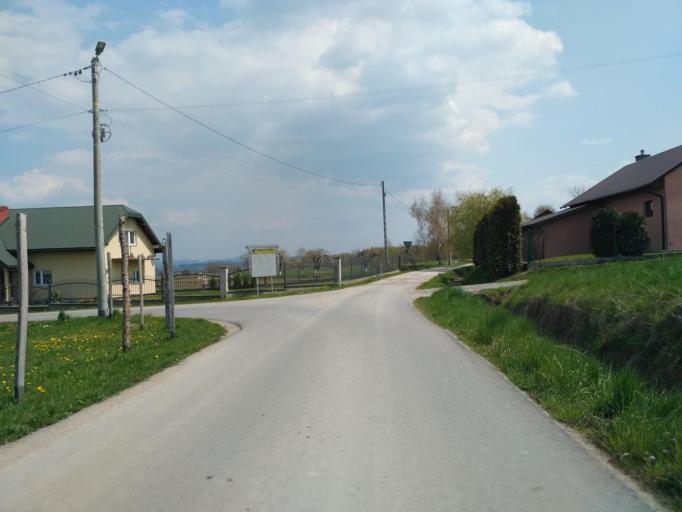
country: PL
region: Subcarpathian Voivodeship
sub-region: Powiat jasielski
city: Jaslo
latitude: 49.7173
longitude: 21.5119
